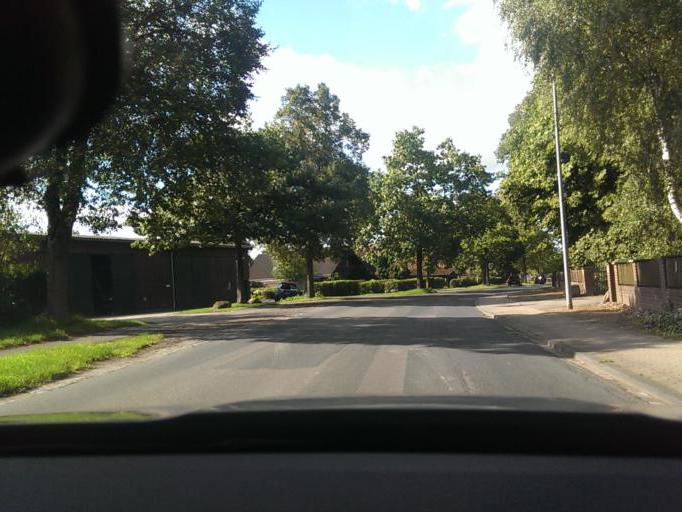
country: DE
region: Lower Saxony
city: Isernhagen Farster Bauerschaft
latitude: 52.4657
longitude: 9.8272
